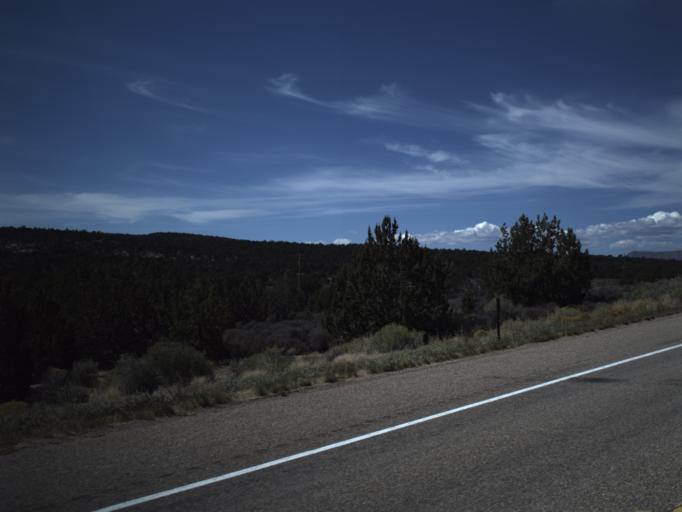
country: US
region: Utah
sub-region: Washington County
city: Ivins
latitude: 37.2741
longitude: -113.6455
